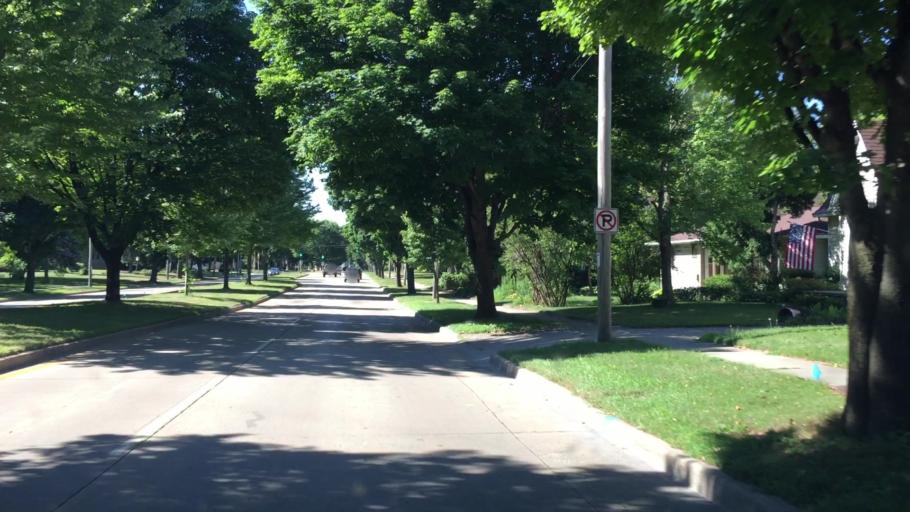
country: US
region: Wisconsin
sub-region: Outagamie County
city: Appleton
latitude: 44.2493
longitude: -88.4158
